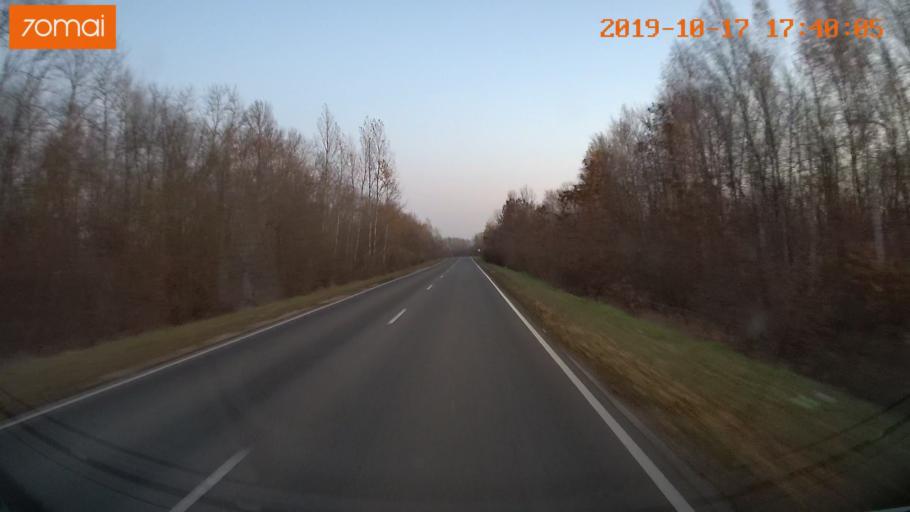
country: RU
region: Tula
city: Yepifan'
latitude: 53.7964
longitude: 38.6022
